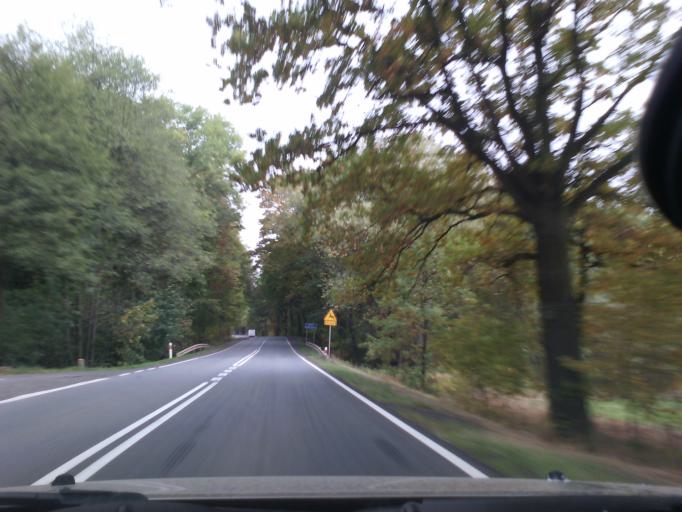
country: PL
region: Lower Silesian Voivodeship
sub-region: Powiat swidnicki
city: Swiebodzice
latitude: 50.8763
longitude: 16.2828
